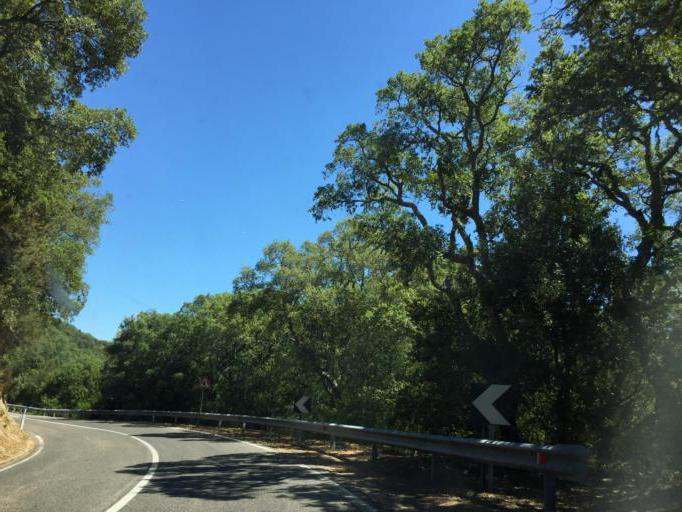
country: IT
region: Sardinia
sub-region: Provincia di Olbia-Tempio
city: Calangianus
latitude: 40.8932
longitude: 9.2635
